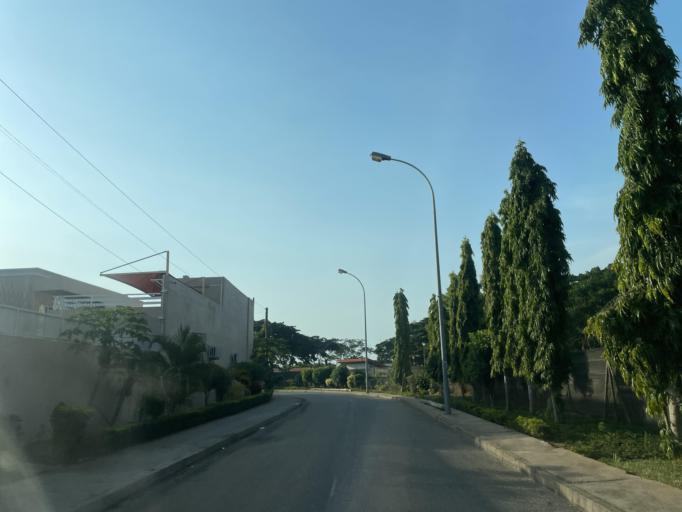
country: AO
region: Luanda
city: Luanda
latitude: -8.9127
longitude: 13.1815
